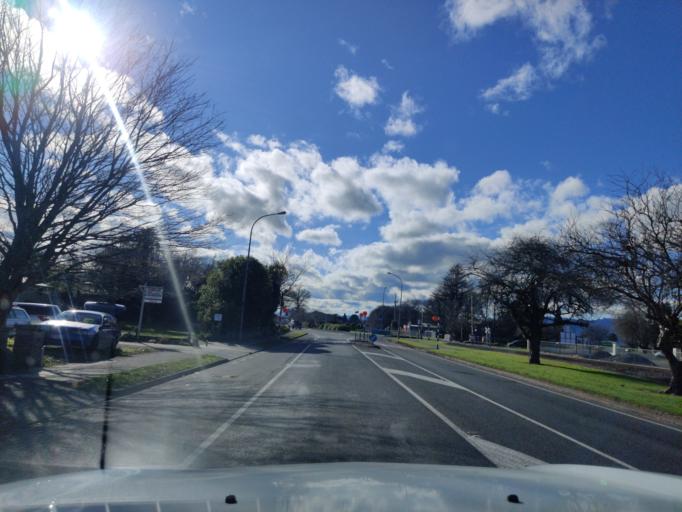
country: NZ
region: Waikato
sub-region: Matamata-Piako District
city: Matamata
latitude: -37.8155
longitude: 175.7711
